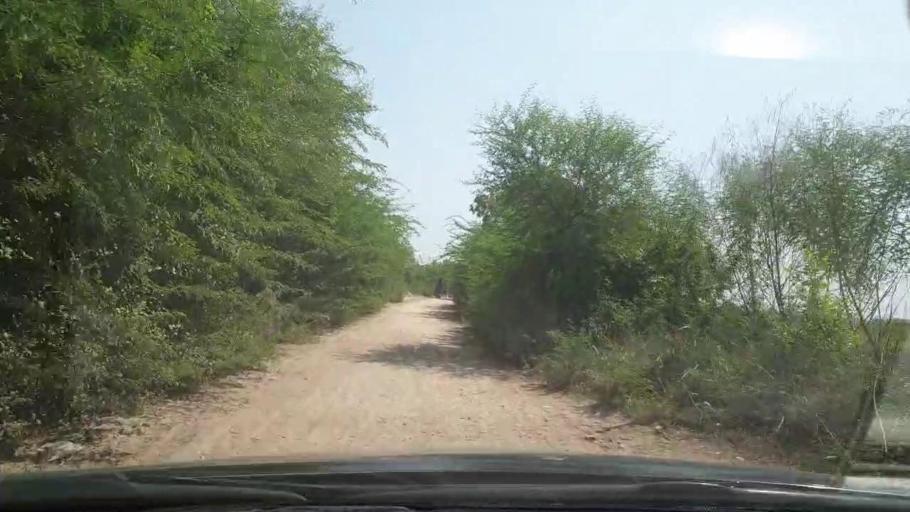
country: PK
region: Sindh
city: Tando Bago
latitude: 24.7732
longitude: 69.1897
